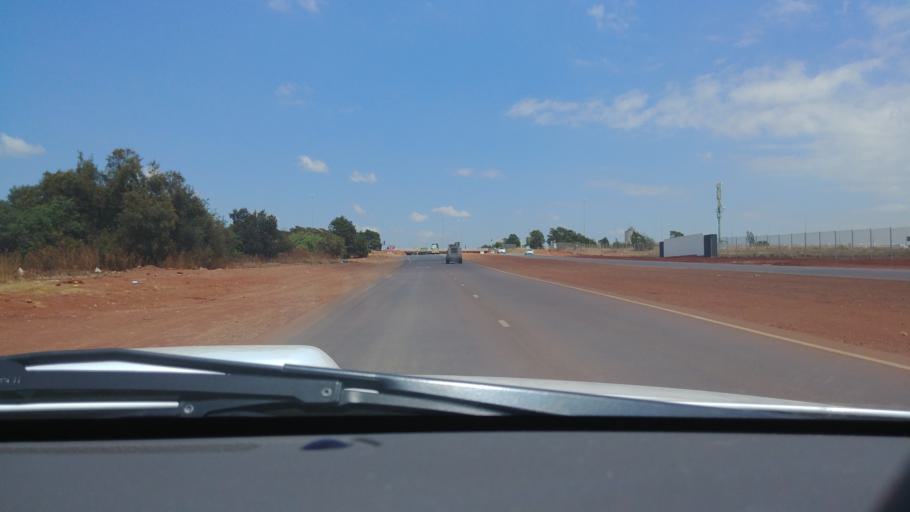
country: ZA
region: Gauteng
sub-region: Ekurhuleni Metropolitan Municipality
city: Tembisa
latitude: -26.0297
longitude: 28.2713
